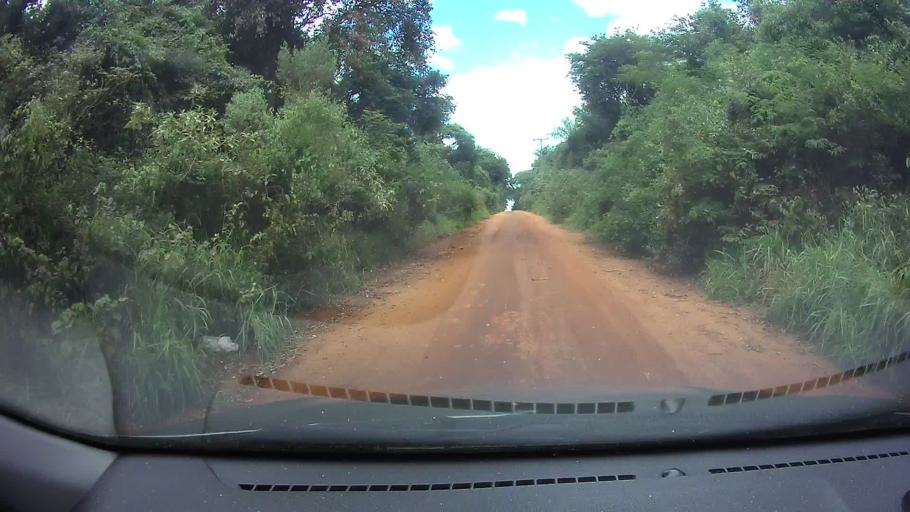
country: PY
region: Paraguari
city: La Colmena
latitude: -25.9445
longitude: -56.7800
